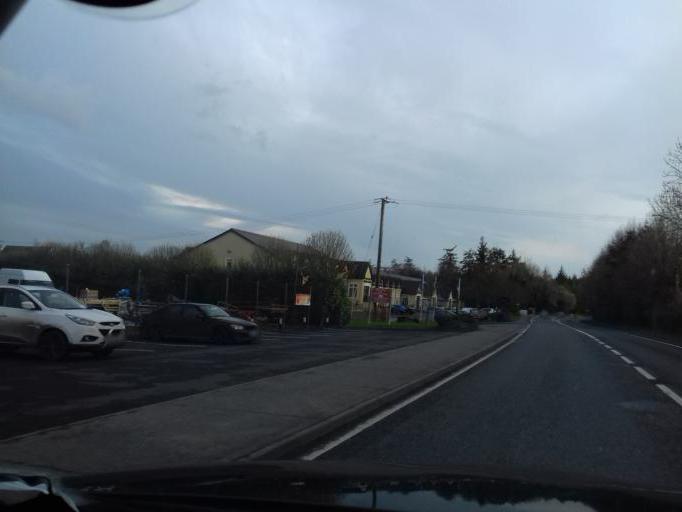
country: IE
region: Leinster
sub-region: Laois
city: Abbeyleix
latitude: 52.9075
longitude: -7.3529
